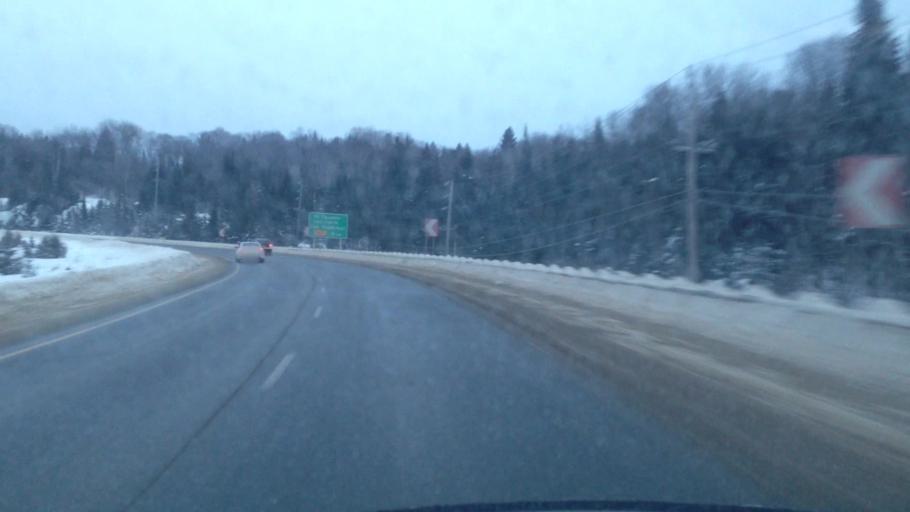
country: CA
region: Quebec
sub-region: Laurentides
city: Mont-Tremblant
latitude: 46.1091
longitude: -74.5130
